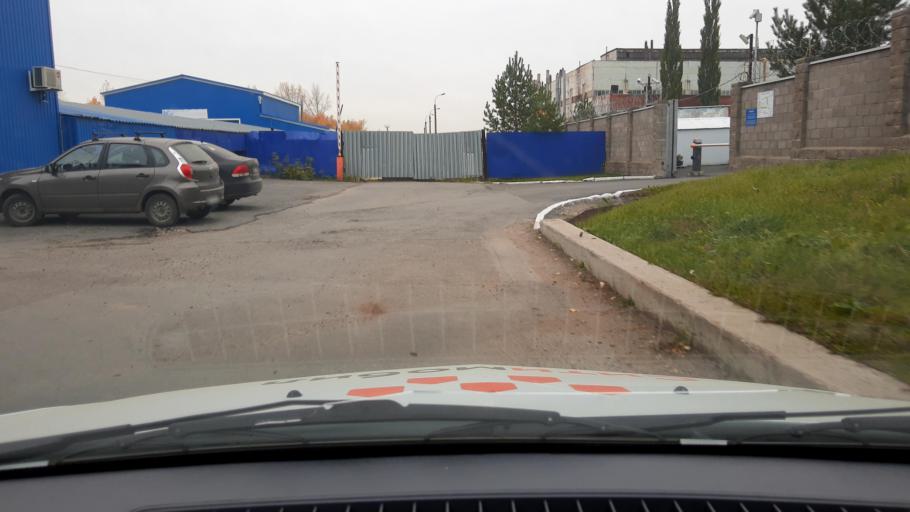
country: RU
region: Bashkortostan
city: Ufa
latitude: 54.8072
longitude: 56.0612
